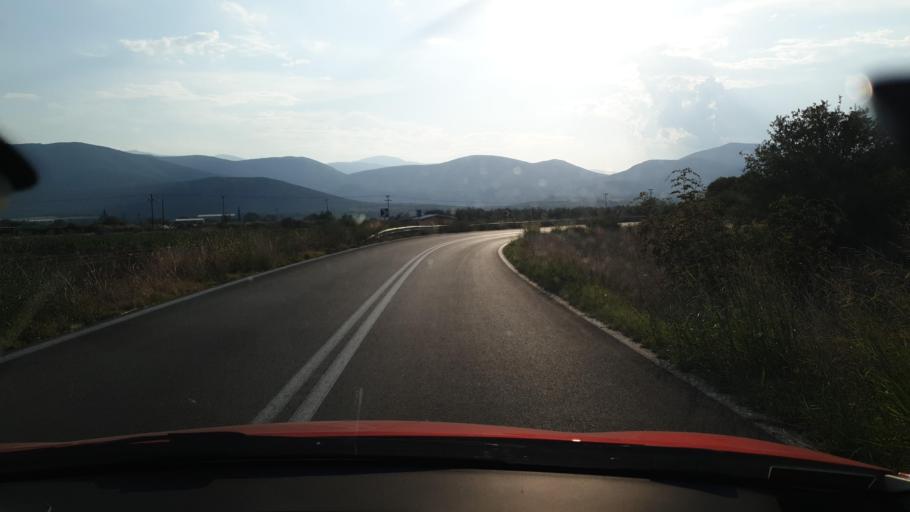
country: GR
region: Thessaly
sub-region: Nomos Magnisias
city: Sourpi
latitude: 39.1095
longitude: 22.8850
